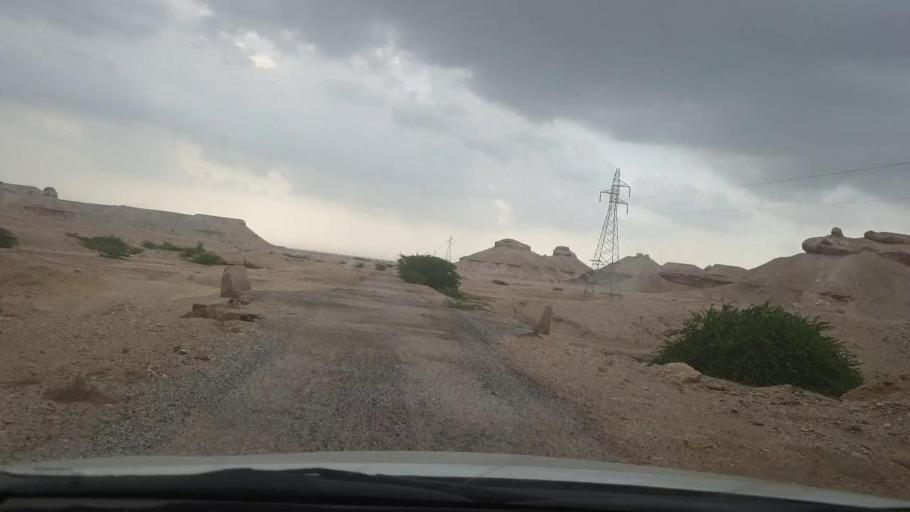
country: PK
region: Sindh
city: Khairpur
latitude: 27.4700
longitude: 68.8986
